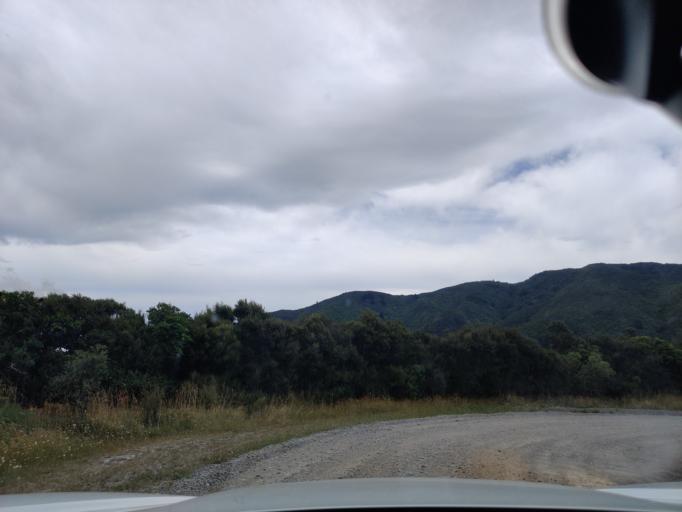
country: NZ
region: Wellington
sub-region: Masterton District
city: Masterton
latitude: -41.0416
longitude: 175.4065
